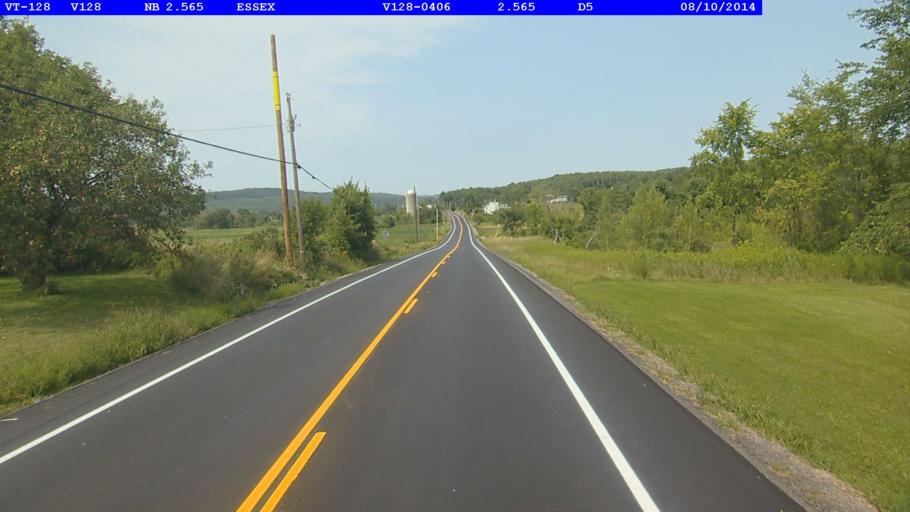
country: US
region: Vermont
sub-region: Chittenden County
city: Jericho
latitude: 44.5347
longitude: -73.0314
